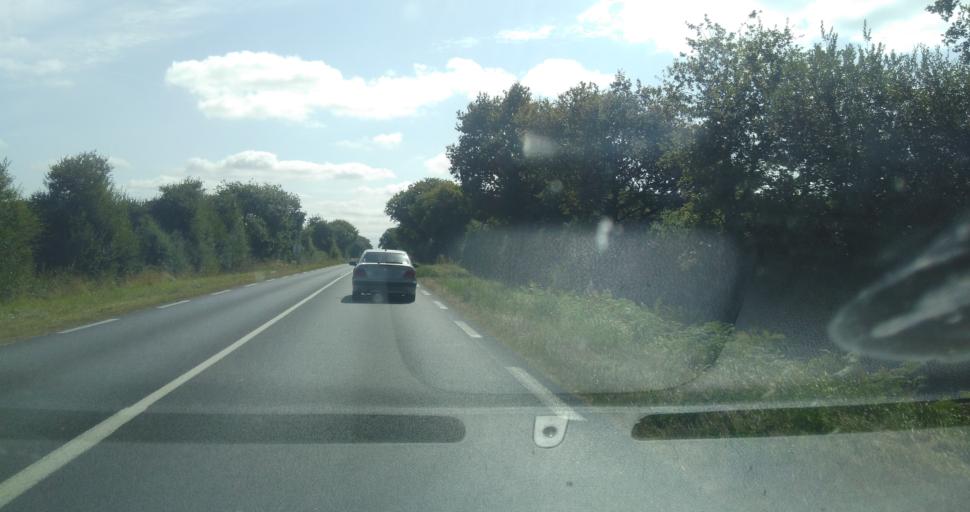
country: FR
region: Pays de la Loire
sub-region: Departement de la Vendee
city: Chateau-d'Olonne
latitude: 46.4785
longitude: -1.6849
